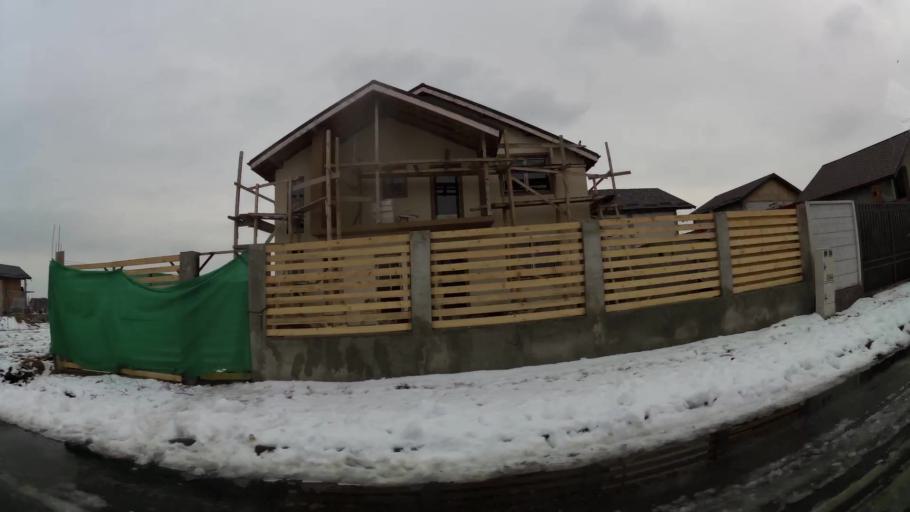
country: RO
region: Ilfov
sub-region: Comuna Tunari
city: Tunari
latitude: 44.5525
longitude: 26.1571
